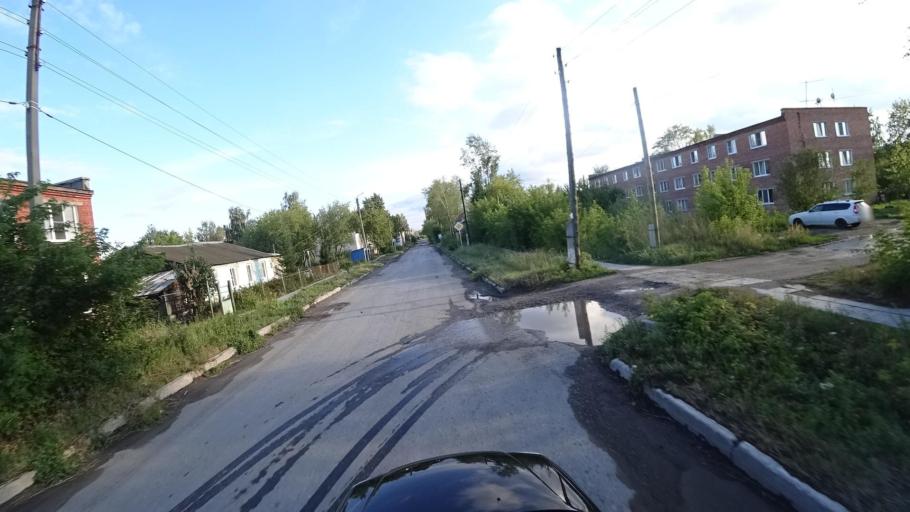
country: RU
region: Sverdlovsk
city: Kamyshlov
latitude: 56.8544
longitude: 62.7296
